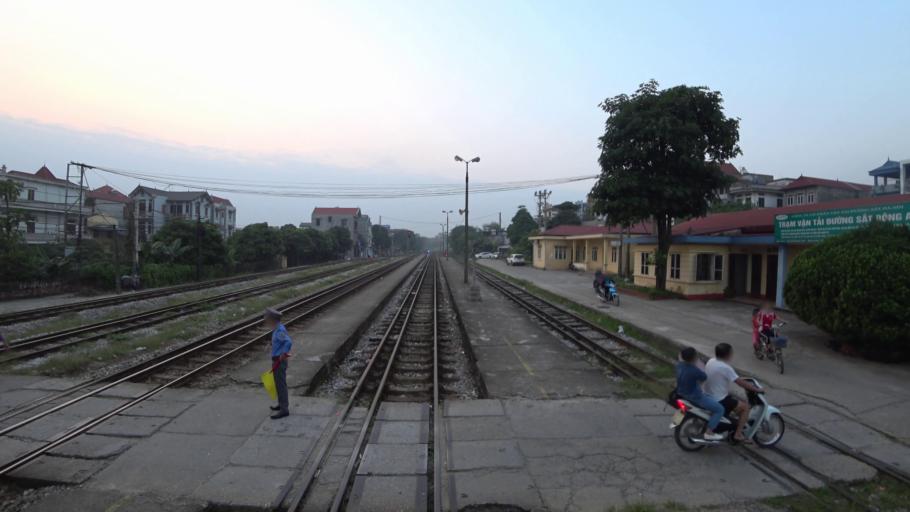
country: VN
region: Ha Noi
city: Dong Anh
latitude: 21.1620
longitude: 105.8476
